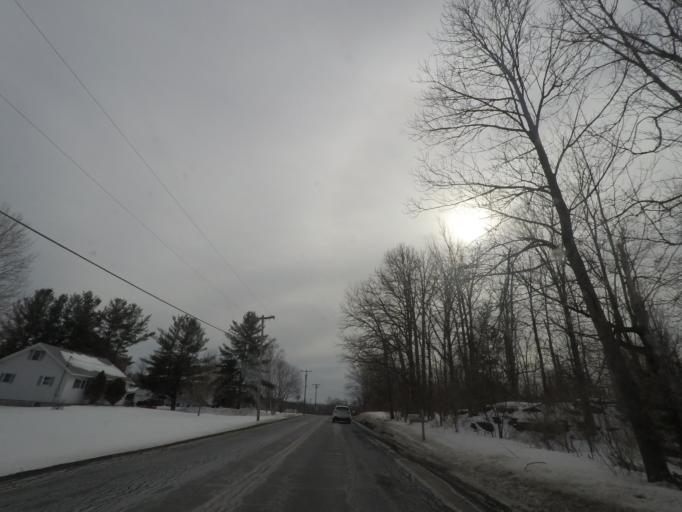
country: US
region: New York
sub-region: Albany County
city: Altamont
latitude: 42.6646
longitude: -74.1318
